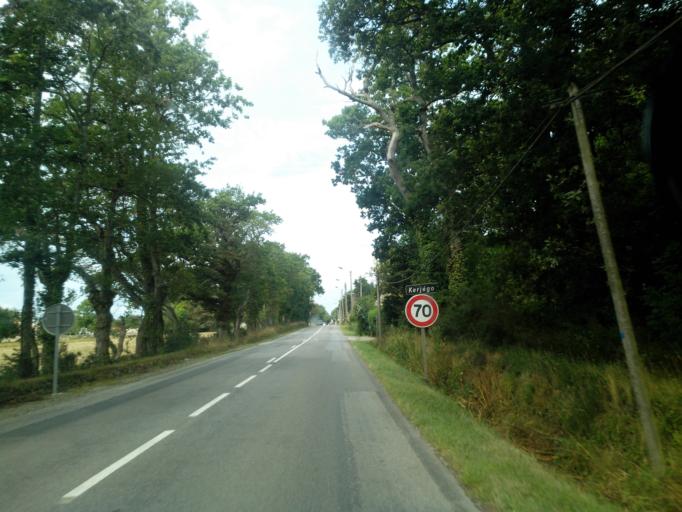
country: FR
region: Brittany
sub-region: Departement du Morbihan
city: Auray
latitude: 47.6661
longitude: -3.0320
